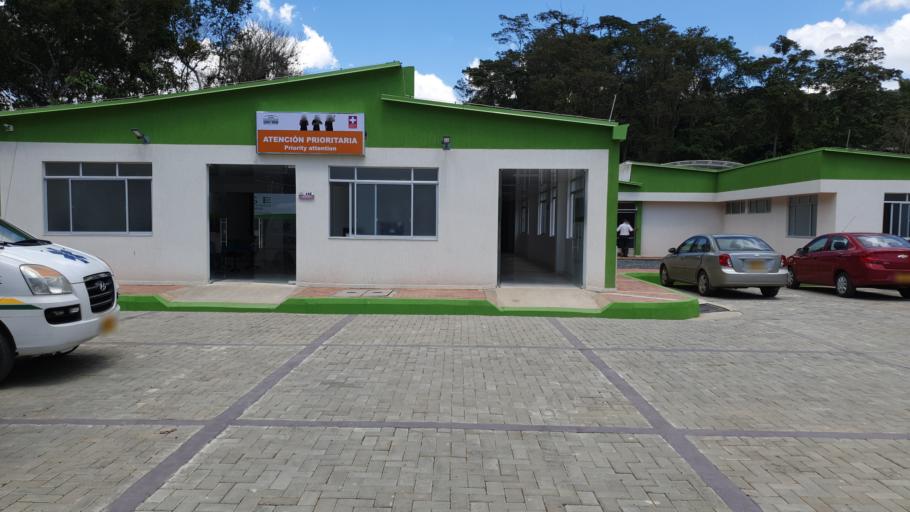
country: CO
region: Boyaca
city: Santana
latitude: 6.0525
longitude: -73.4874
